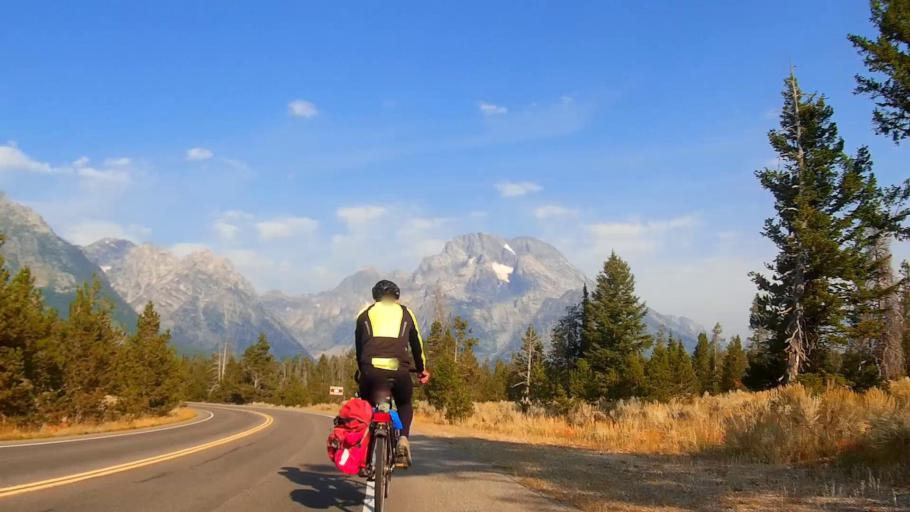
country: US
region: Wyoming
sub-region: Teton County
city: Moose Wilson Road
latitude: 43.7932
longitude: -110.7043
